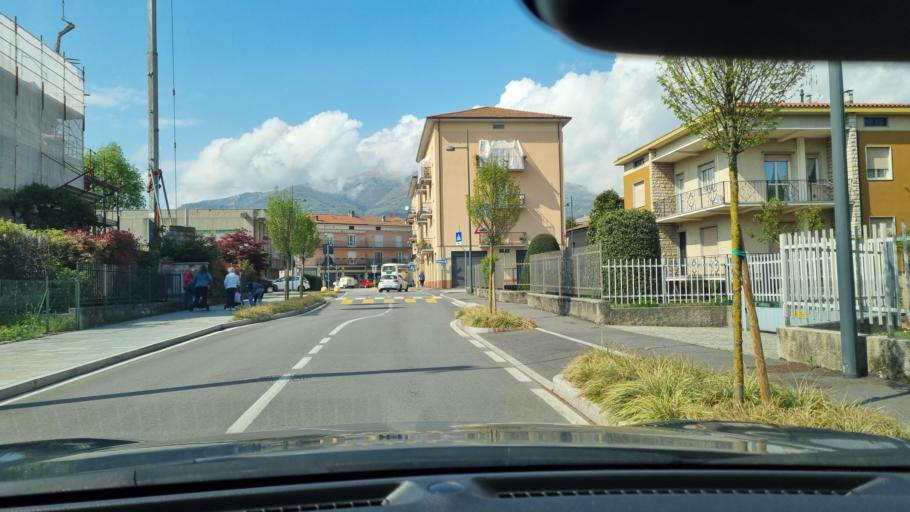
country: IT
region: Lombardy
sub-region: Provincia di Bergamo
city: Ambivere
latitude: 45.7194
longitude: 9.5494
